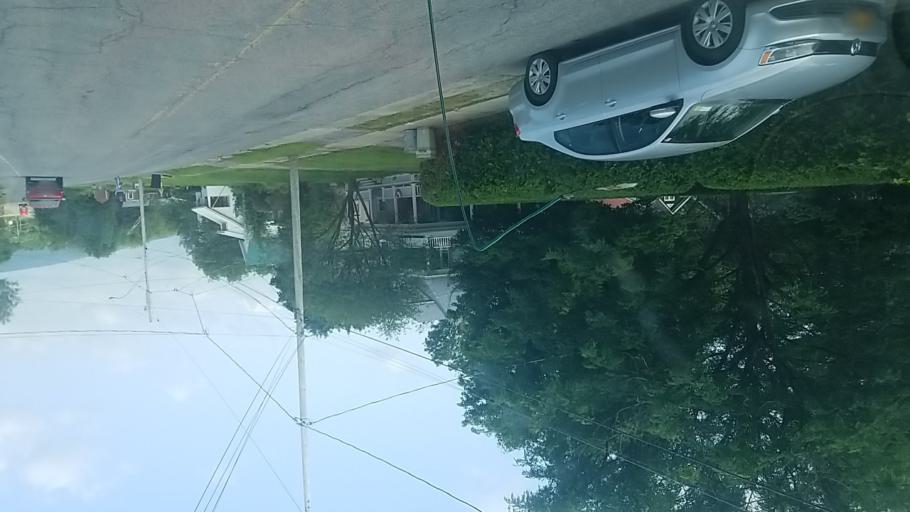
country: US
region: New York
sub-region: Fulton County
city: Broadalbin
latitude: 43.1045
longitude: -74.2673
